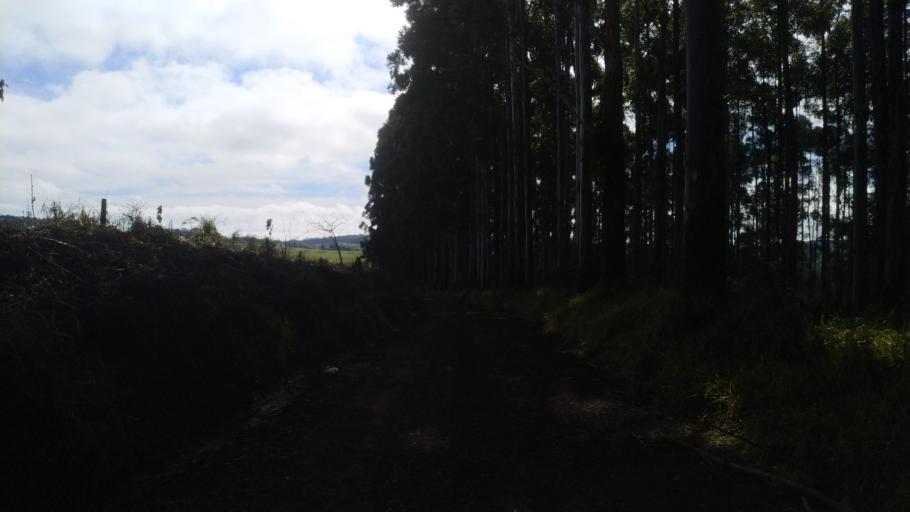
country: BR
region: Santa Catarina
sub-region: Chapeco
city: Chapeco
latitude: -27.1594
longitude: -52.5968
